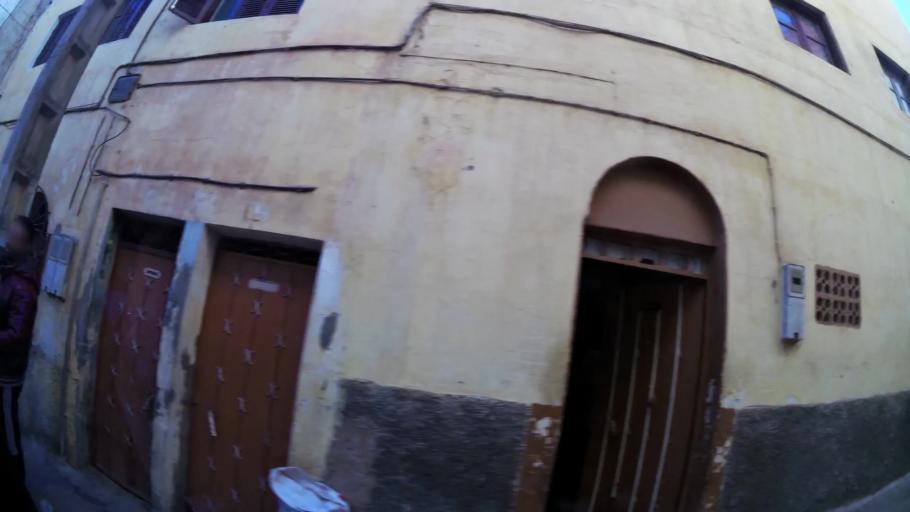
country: MA
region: Chaouia-Ouardigha
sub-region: Settat Province
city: Settat
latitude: 32.9993
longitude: -7.6078
